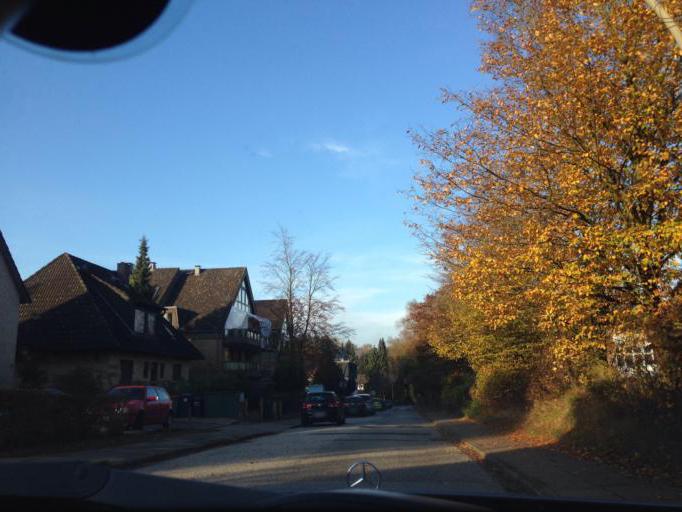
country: DE
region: Schleswig-Holstein
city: Barsbuettel
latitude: 53.5924
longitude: 10.1790
